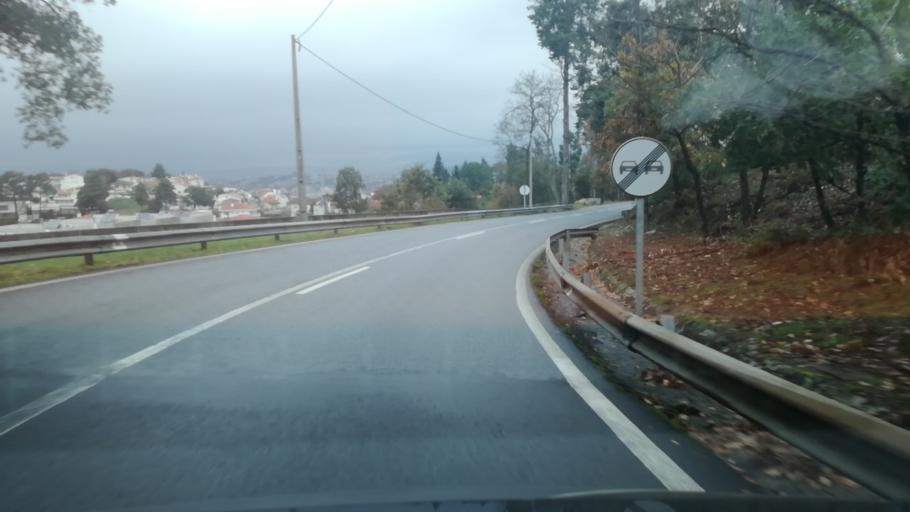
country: PT
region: Braga
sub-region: Braga
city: Braga
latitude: 41.5300
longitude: -8.3942
